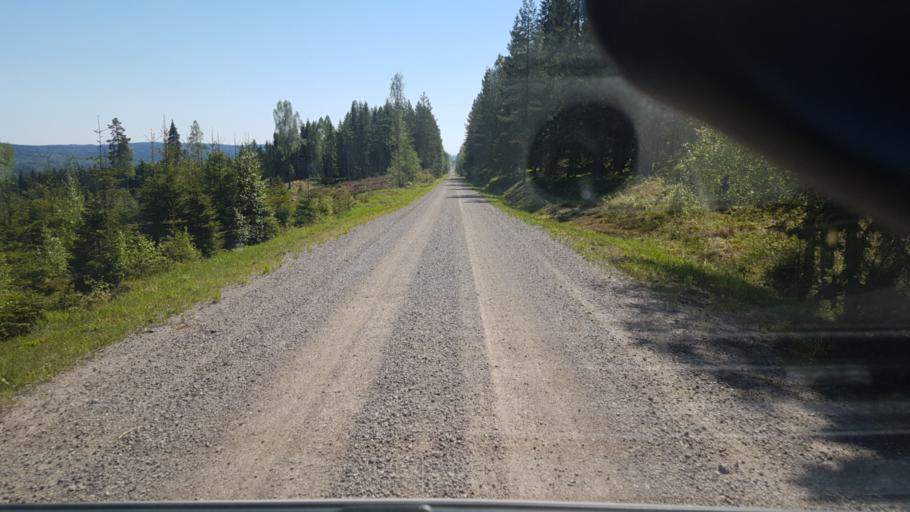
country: SE
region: Vaermland
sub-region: Eda Kommun
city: Charlottenberg
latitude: 60.0074
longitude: 12.5066
